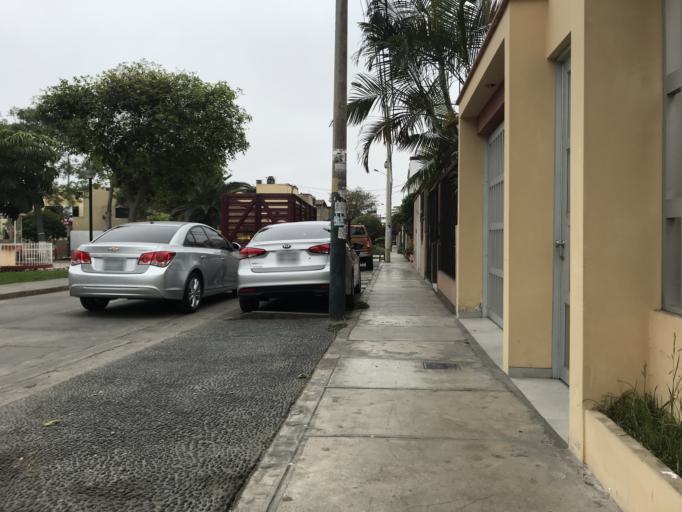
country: PE
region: Lima
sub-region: Lima
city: San Isidro
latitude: -12.0780
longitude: -77.0718
